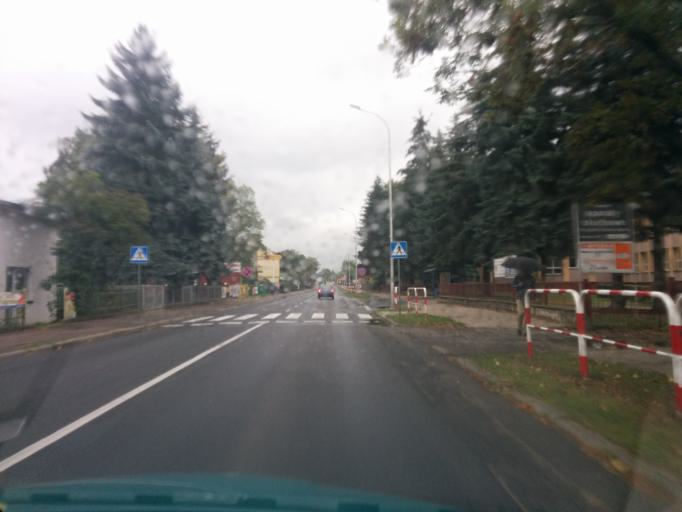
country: PL
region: Subcarpathian Voivodeship
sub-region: Powiat sanocki
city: Sanok
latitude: 49.5539
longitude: 22.2080
